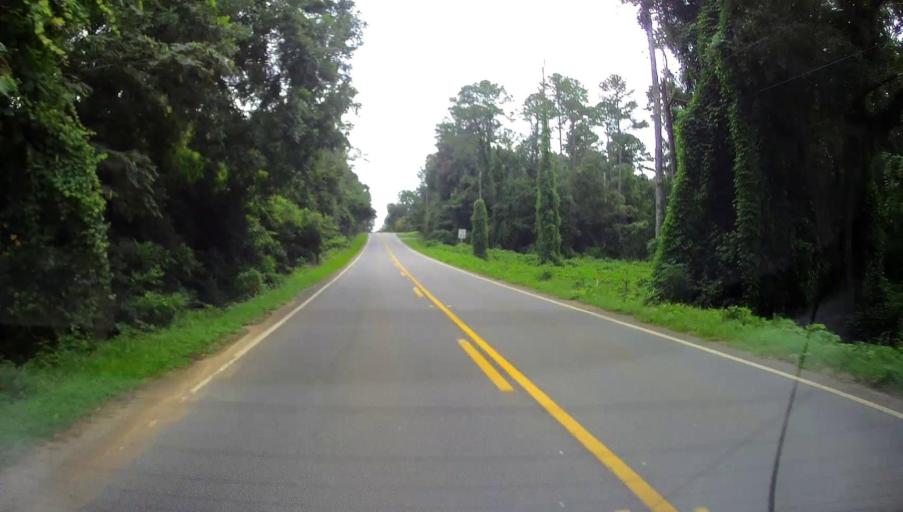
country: US
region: Georgia
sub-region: Schley County
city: Ellaville
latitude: 32.2425
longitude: -84.3184
